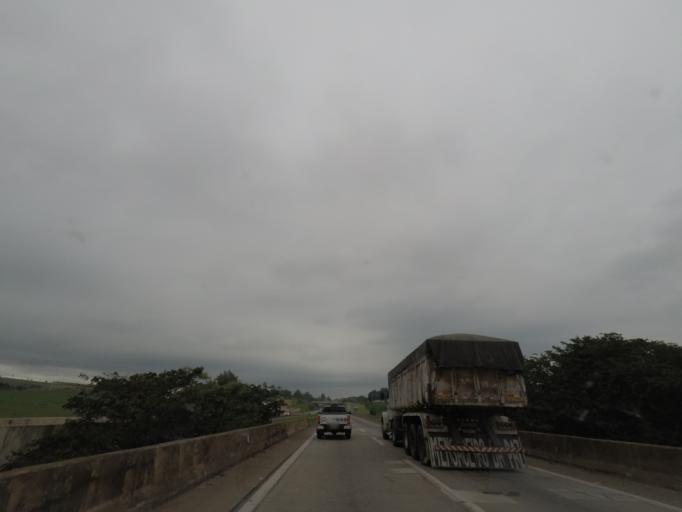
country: BR
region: Sao Paulo
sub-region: Jarinu
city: Jarinu
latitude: -23.0491
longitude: -46.6686
